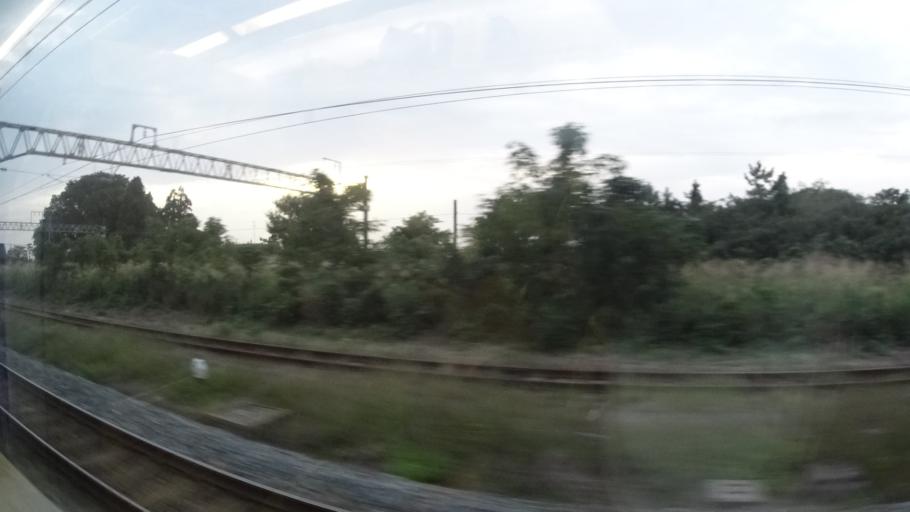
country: JP
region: Niigata
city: Murakami
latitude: 38.1185
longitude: 139.4451
